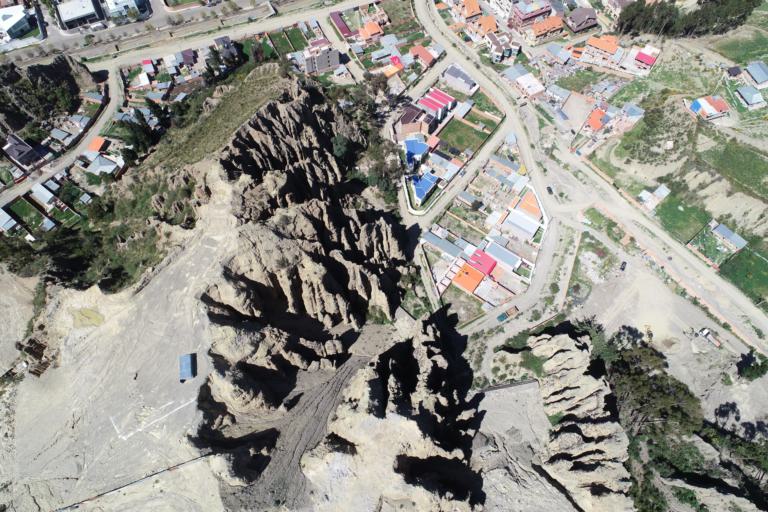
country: BO
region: La Paz
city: La Paz
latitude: -16.5076
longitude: -68.0569
